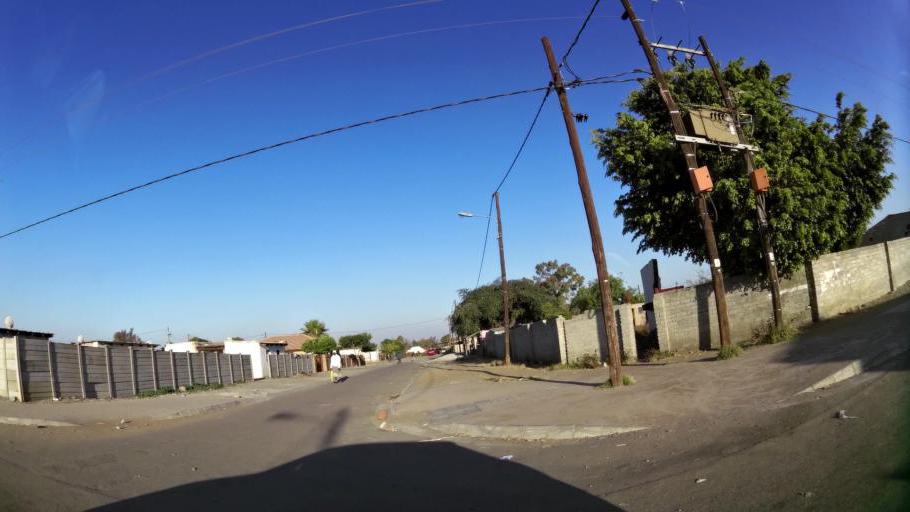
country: ZA
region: North-West
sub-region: Bojanala Platinum District Municipality
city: Rustenburg
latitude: -25.6371
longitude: 27.2191
